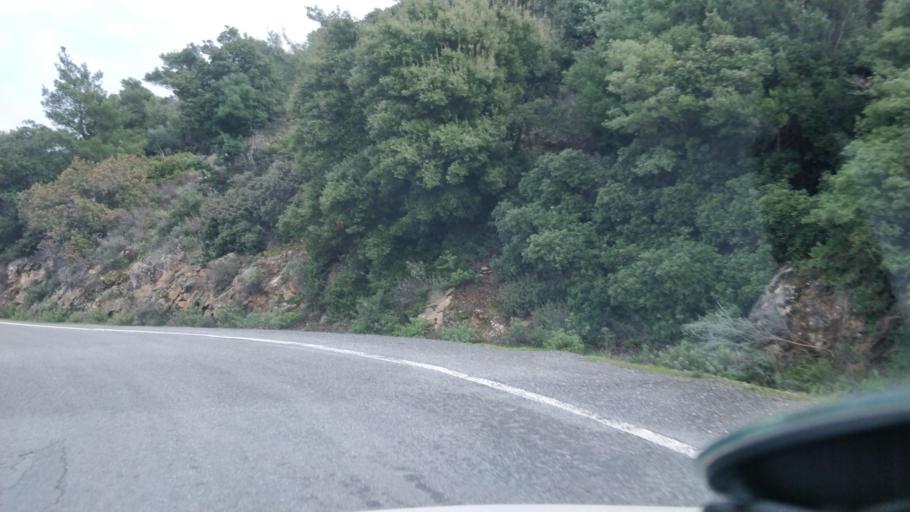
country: GR
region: Crete
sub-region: Nomos Lasithiou
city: Agios Nikolaos
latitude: 35.1074
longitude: 25.7129
